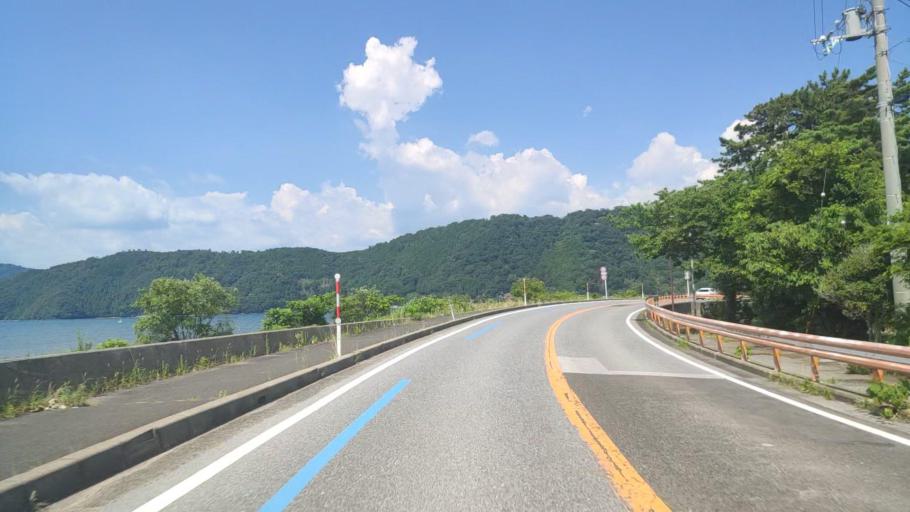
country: JP
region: Shiga Prefecture
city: Nagahama
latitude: 35.4503
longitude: 136.1902
